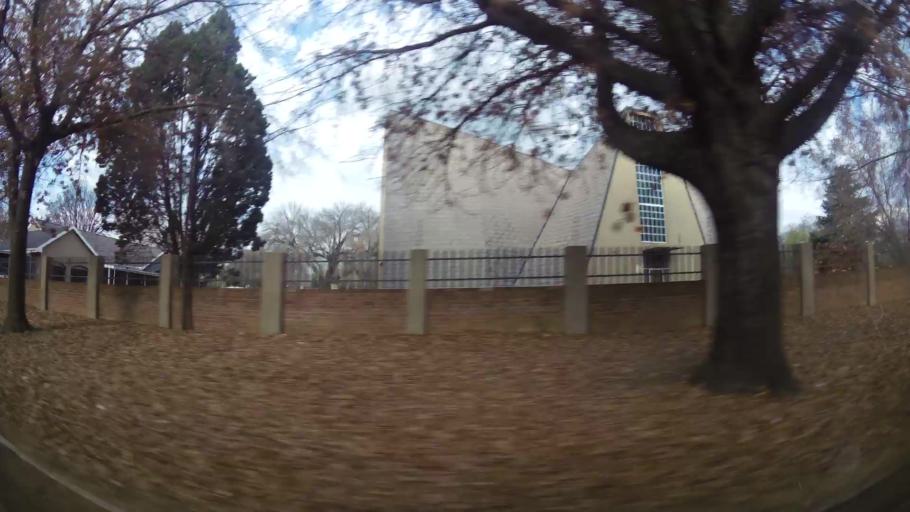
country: ZA
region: Orange Free State
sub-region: Fezile Dabi District Municipality
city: Sasolburg
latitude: -26.8021
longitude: 27.8180
